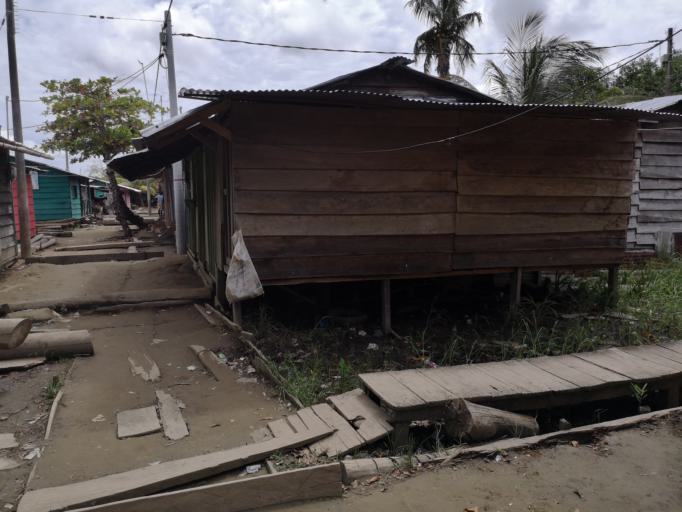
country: CO
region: Antioquia
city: Turbo
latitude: 8.0877
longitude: -76.8389
